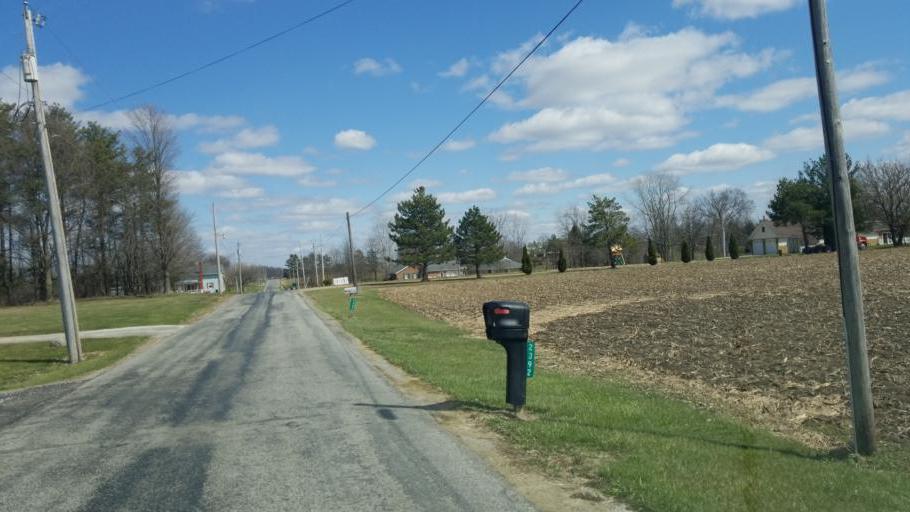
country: US
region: Ohio
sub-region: Richland County
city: Shelby
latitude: 40.8864
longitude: -82.6207
